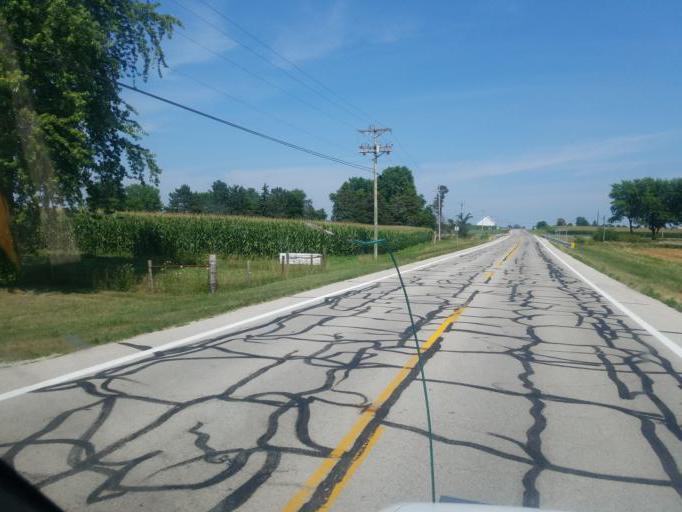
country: US
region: Ohio
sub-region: Auglaize County
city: Saint Marys
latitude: 40.4948
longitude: -84.4576
